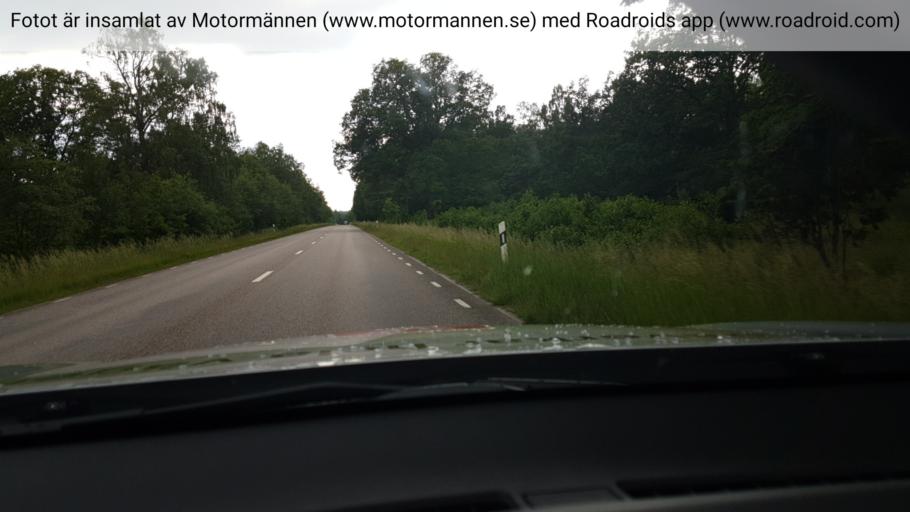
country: SE
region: Vaestra Goetaland
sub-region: Hjo Kommun
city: Hjo
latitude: 58.2624
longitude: 14.2527
